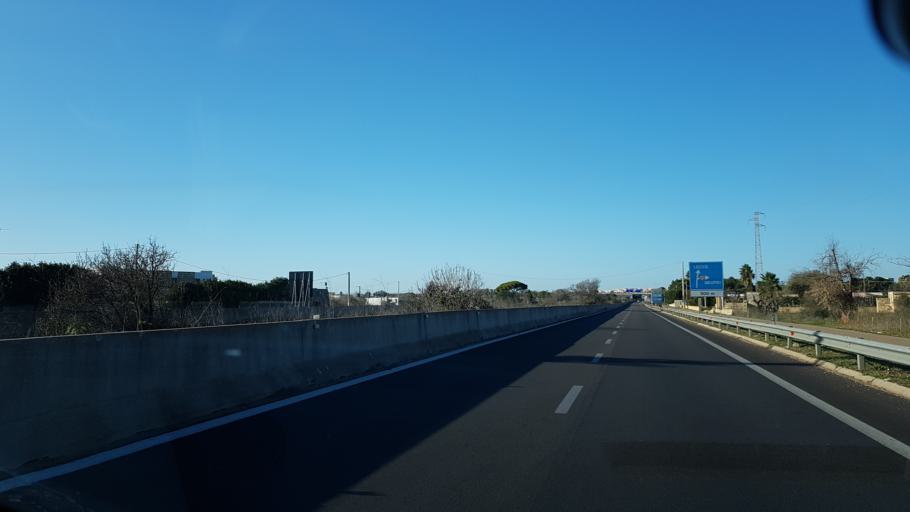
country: IT
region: Apulia
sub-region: Provincia di Lecce
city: Gallipoli
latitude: 40.0359
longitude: 18.0256
